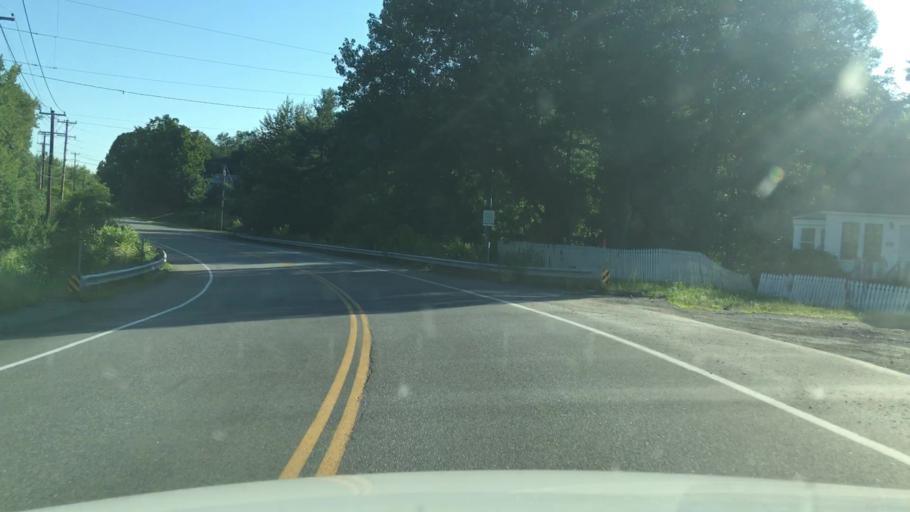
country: US
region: Maine
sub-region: Penobscot County
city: Veazie
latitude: 44.8189
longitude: -68.7298
